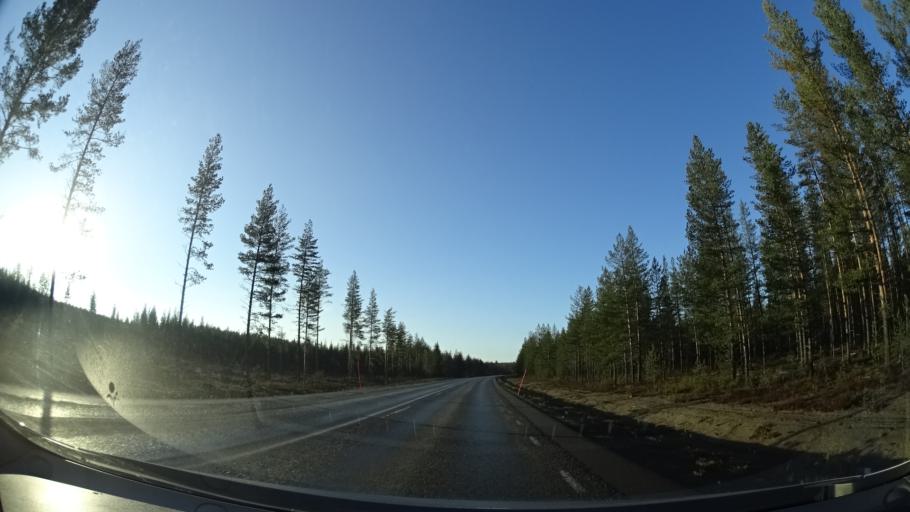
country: SE
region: Vaesterbotten
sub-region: Norsjo Kommun
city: Norsjoe
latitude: 64.9833
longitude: 19.4988
